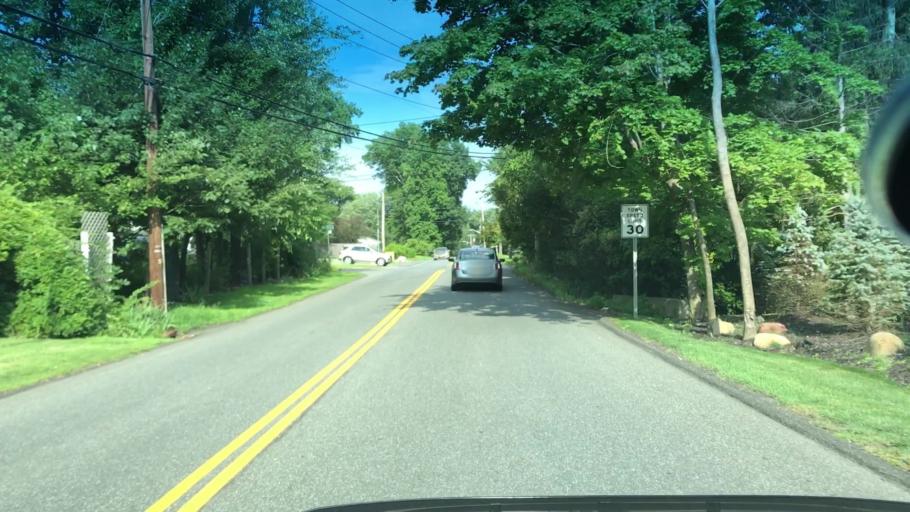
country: US
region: New York
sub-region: Rockland County
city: New Square
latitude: 41.1224
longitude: -74.0150
